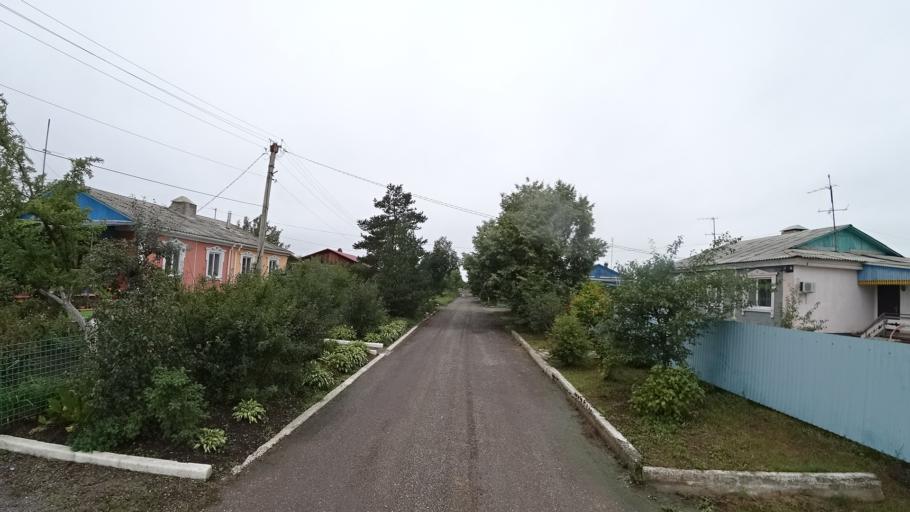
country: RU
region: Primorskiy
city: Monastyrishche
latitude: 44.2037
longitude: 132.4289
